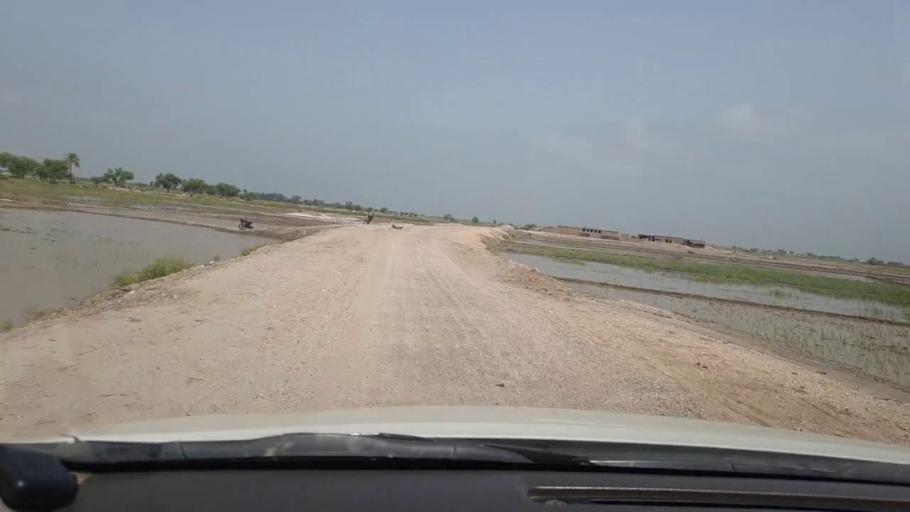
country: PK
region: Sindh
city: Shikarpur
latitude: 28.0002
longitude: 68.5594
